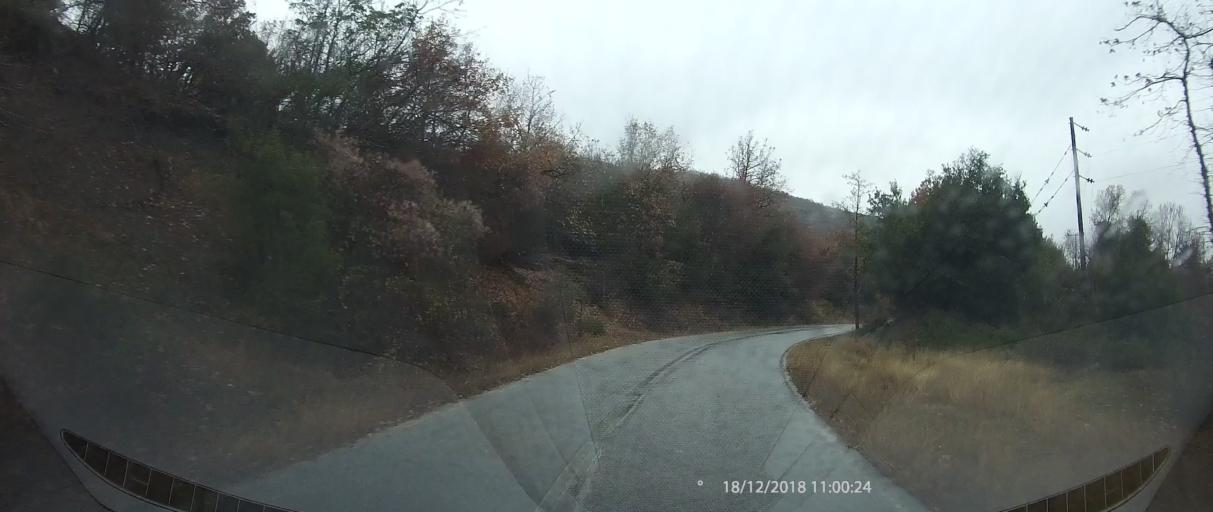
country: GR
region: Central Macedonia
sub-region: Nomos Pierias
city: Kato Milia
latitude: 40.1982
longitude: 22.3172
